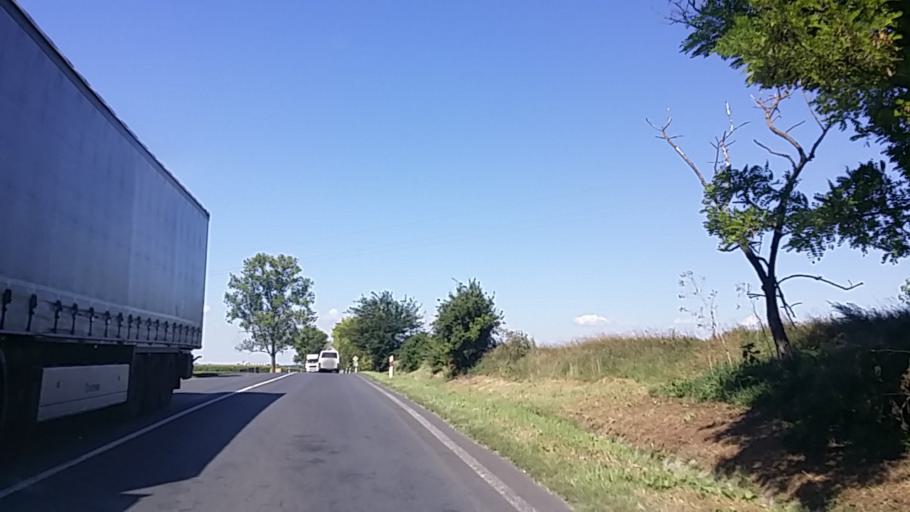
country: HU
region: Fejer
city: Cece
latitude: 46.7647
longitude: 18.5939
